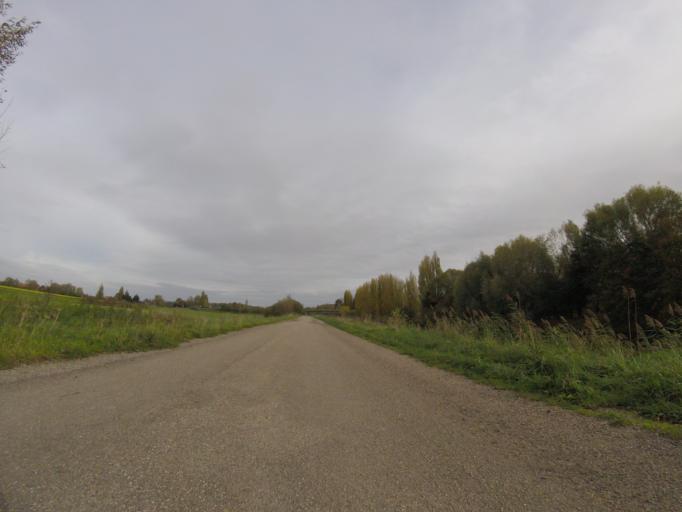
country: FR
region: Nord-Pas-de-Calais
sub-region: Departement du Nord
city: Erquinghem-Lys
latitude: 50.6774
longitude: 2.8318
